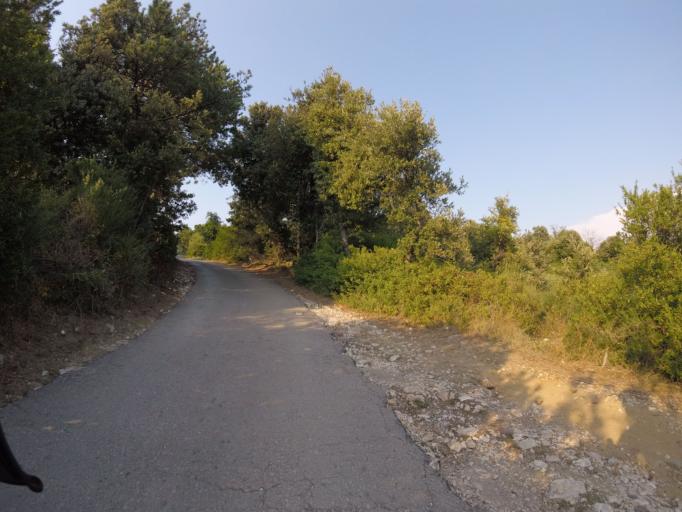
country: HR
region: Primorsko-Goranska
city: Lopar
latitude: 44.8425
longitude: 14.7248
